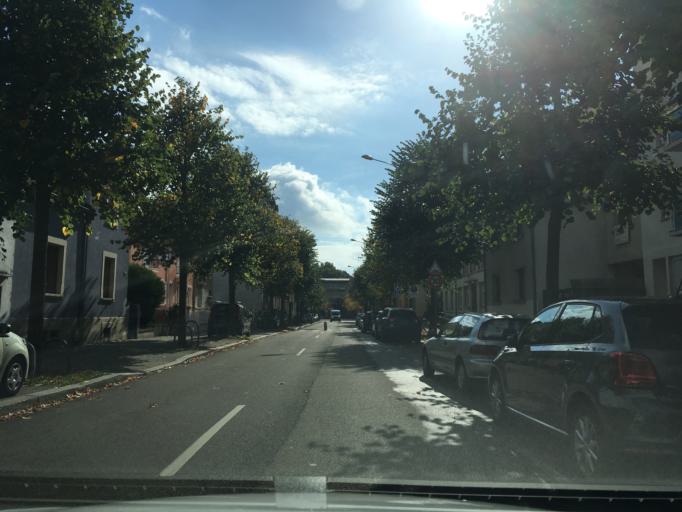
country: FR
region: Alsace
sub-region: Departement du Bas-Rhin
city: Strasbourg
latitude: 48.5652
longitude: 7.7676
